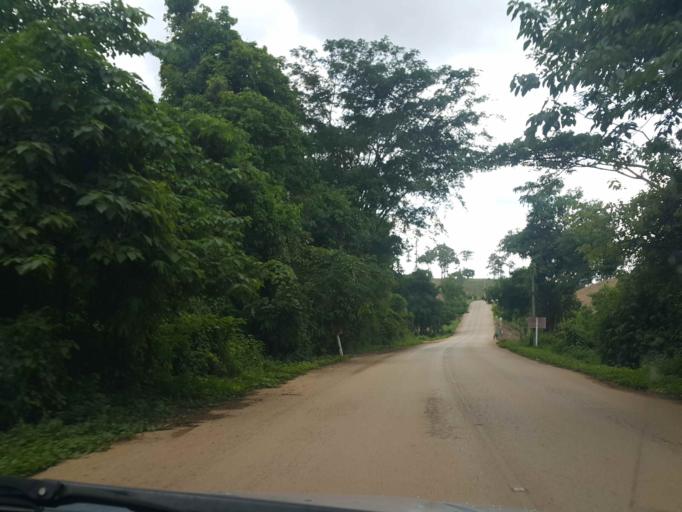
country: TH
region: Lampang
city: Ngao
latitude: 18.9505
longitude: 100.0767
